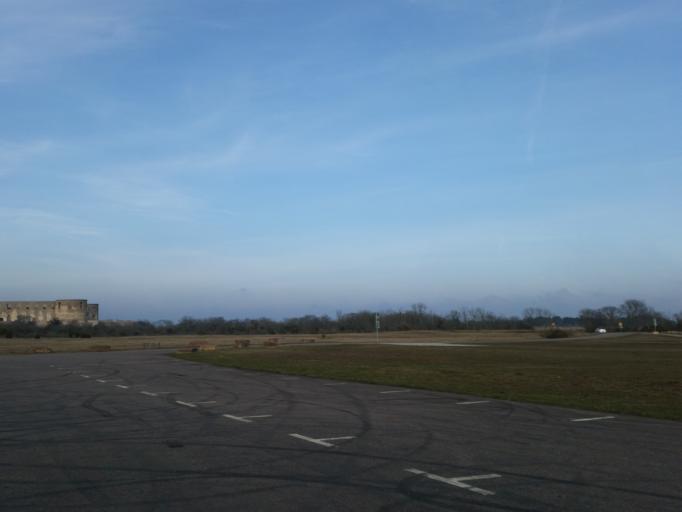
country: SE
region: Kalmar
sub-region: Borgholms Kommun
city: Borgholm
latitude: 56.8663
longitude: 16.6394
